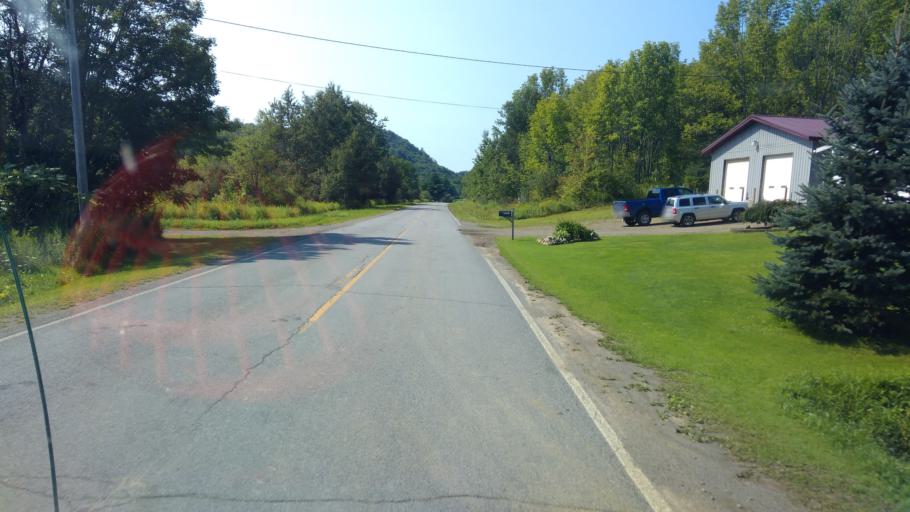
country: US
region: New York
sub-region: Allegany County
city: Bolivar
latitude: 42.1297
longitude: -78.1538
